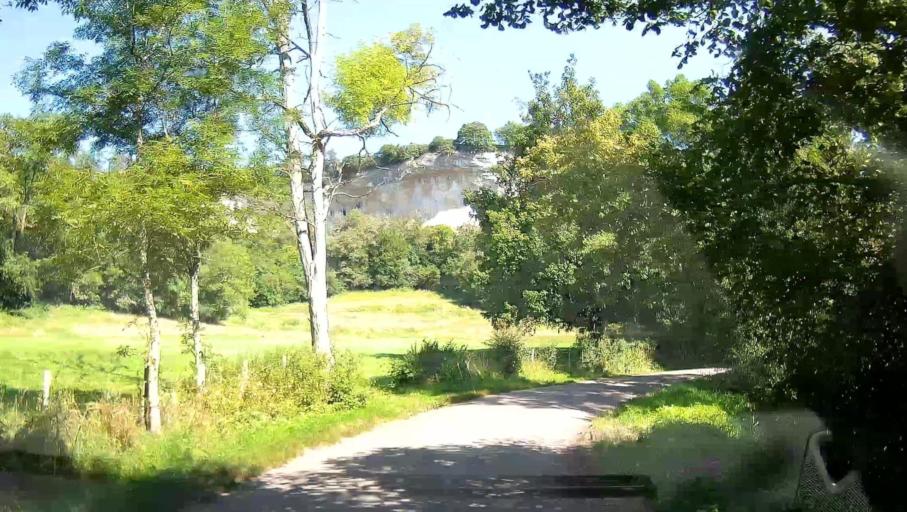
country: FR
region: Bourgogne
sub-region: Departement de la Cote-d'Or
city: Nolay
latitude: 46.9818
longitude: 4.6436
